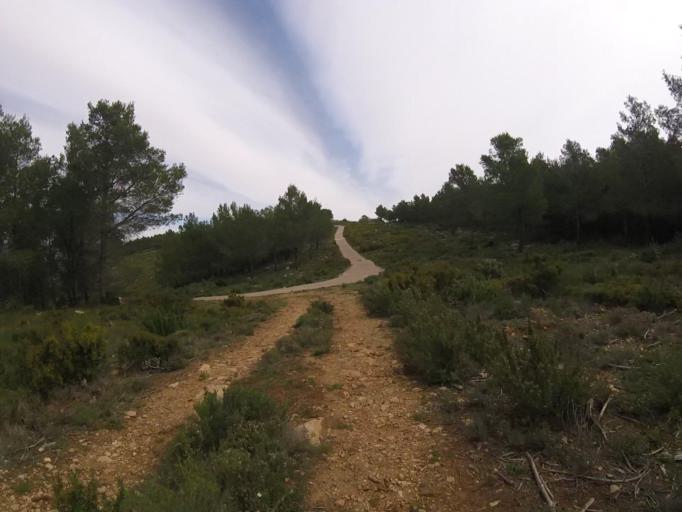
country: ES
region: Valencia
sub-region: Provincia de Castello
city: Cabanes
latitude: 40.1882
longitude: 0.0799
